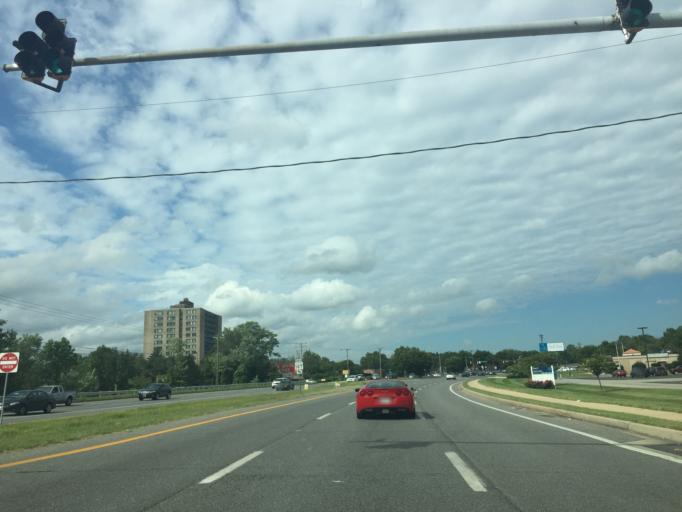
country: US
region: Maryland
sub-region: Prince George's County
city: Laurel
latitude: 39.0956
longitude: -76.8388
